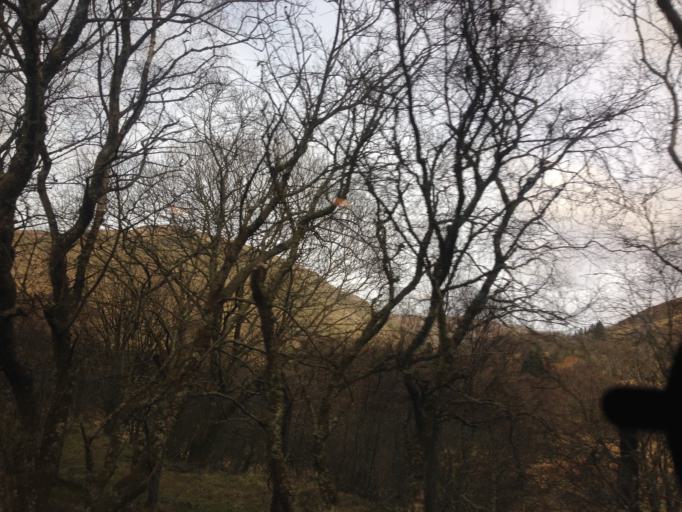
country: GB
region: Scotland
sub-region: Argyll and Bute
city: Garelochhead
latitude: 56.1538
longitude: -4.7805
